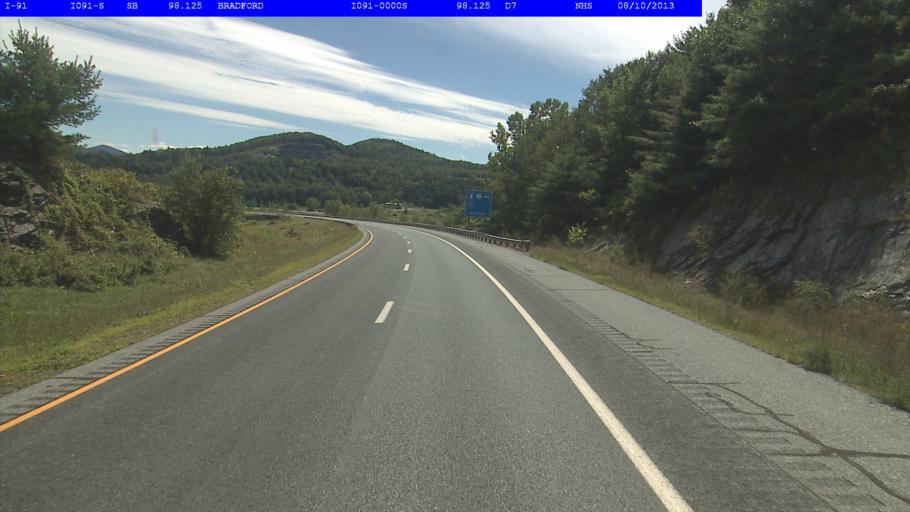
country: US
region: New Hampshire
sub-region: Grafton County
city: Haverhill
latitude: 43.9900
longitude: -72.1358
